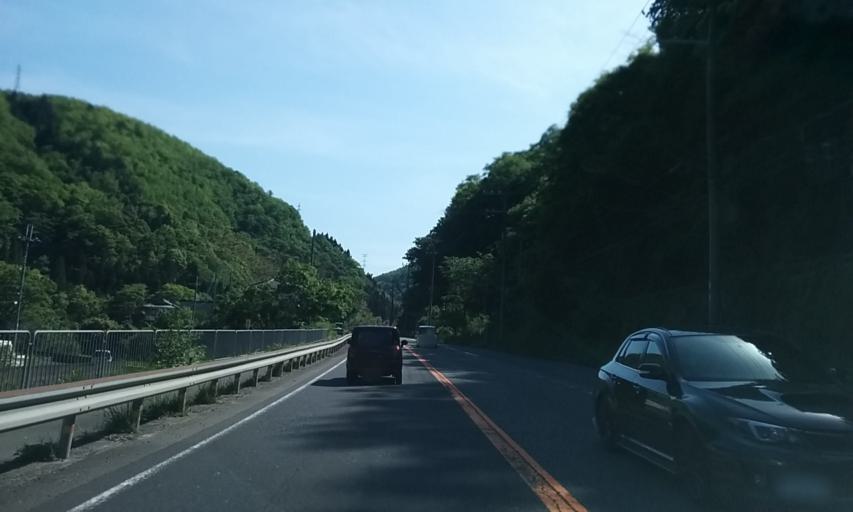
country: JP
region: Kyoto
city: Maizuru
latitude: 35.3925
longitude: 135.3185
